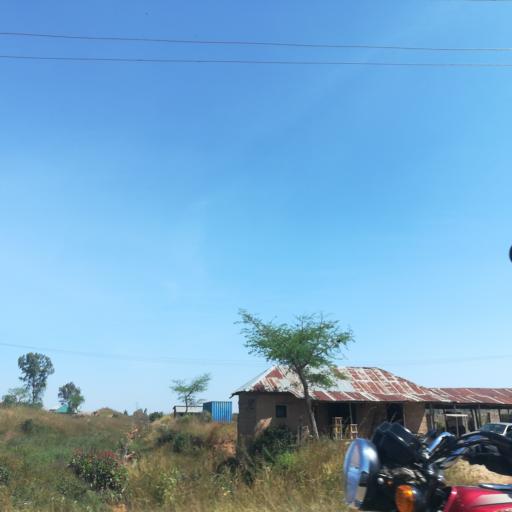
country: NG
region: Plateau
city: Bukuru
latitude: 9.7595
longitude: 8.8633
